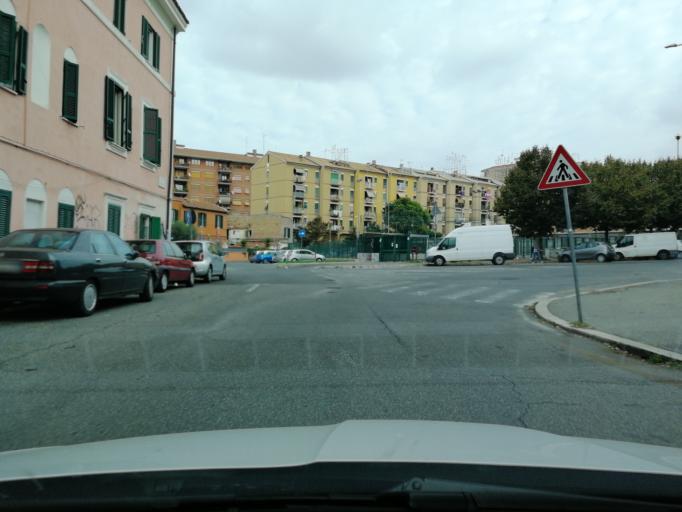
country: IT
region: Latium
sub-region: Citta metropolitana di Roma Capitale
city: Rome
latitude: 41.8599
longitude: 12.5512
